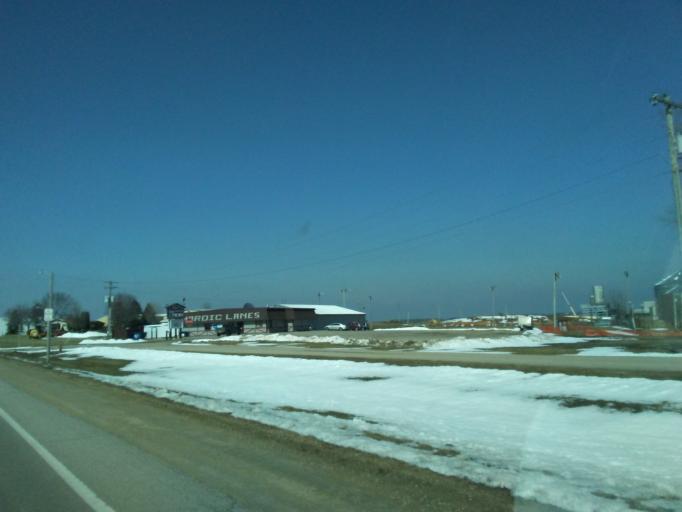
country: US
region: Wisconsin
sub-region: Vernon County
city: Westby
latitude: 43.6605
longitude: -90.8591
